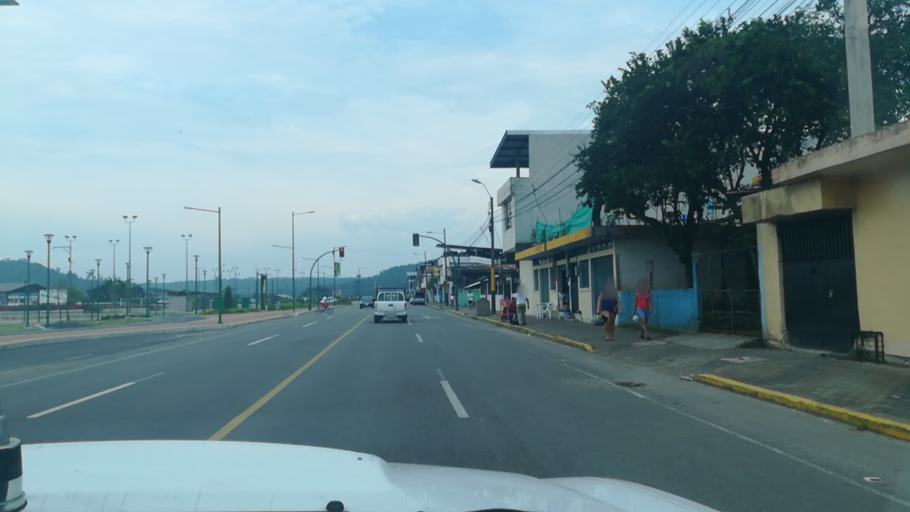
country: EC
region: Napo
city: Tena
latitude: -0.9868
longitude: -77.8207
